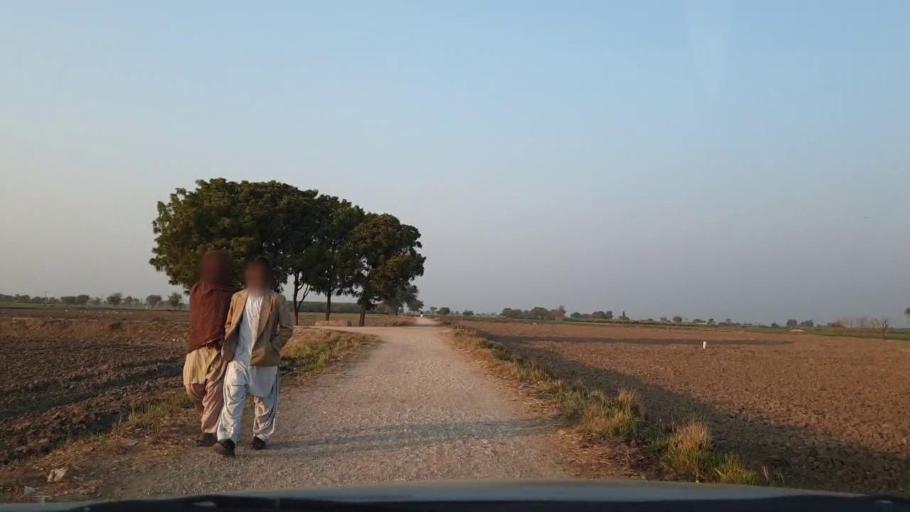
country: PK
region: Sindh
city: Tando Adam
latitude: 25.7139
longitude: 68.5792
